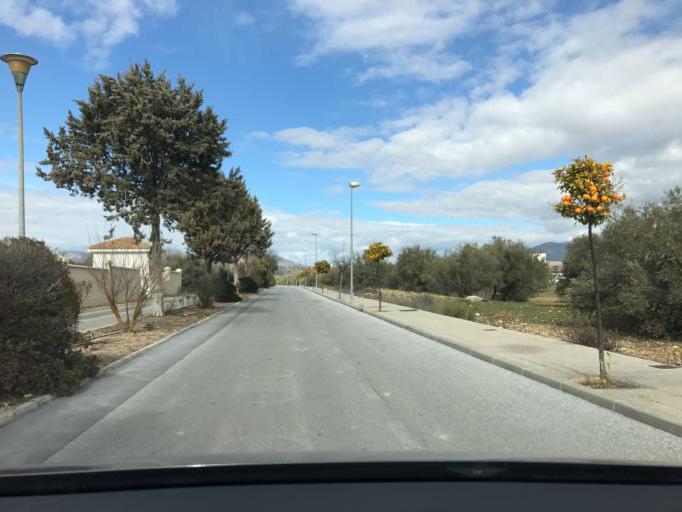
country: ES
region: Andalusia
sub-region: Provincia de Granada
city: Atarfe
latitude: 37.2755
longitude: -3.6949
